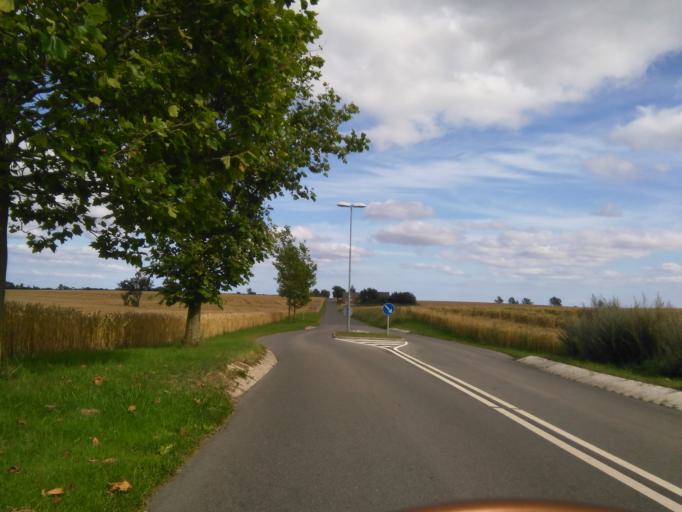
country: DK
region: Central Jutland
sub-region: Skanderborg Kommune
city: Stilling
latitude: 56.0998
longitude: 9.9994
